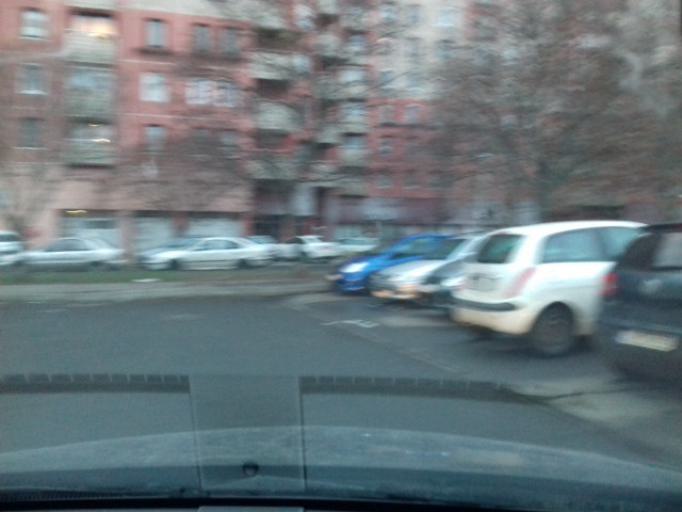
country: HU
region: Budapest
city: Budapest XV. keruelet
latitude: 47.5802
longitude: 19.1158
